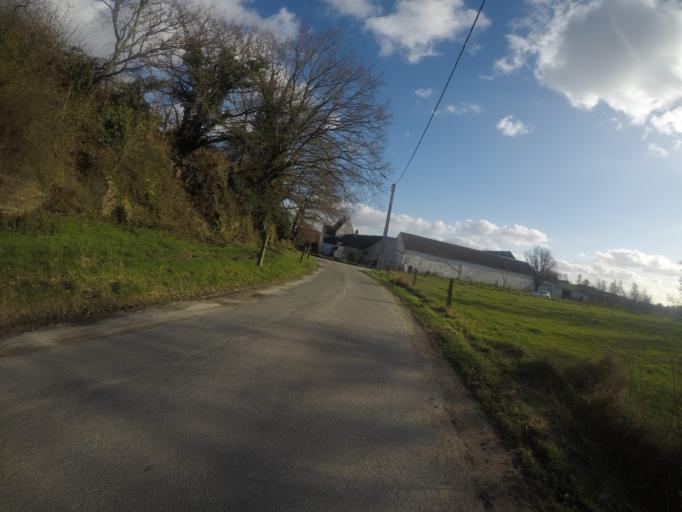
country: BE
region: Wallonia
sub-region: Province du Brabant Wallon
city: Rebecq-Rognon
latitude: 50.6390
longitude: 4.0606
